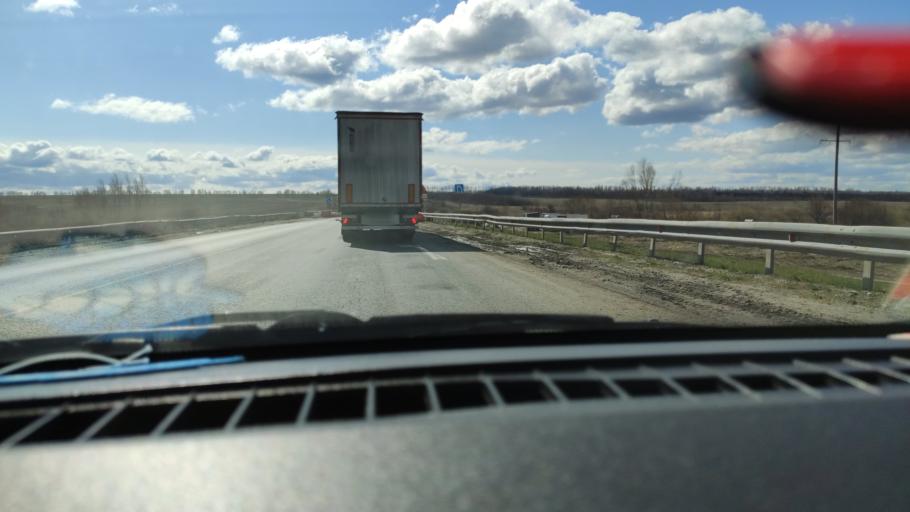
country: RU
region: Saratov
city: Dukhovnitskoye
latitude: 52.7381
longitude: 48.2553
